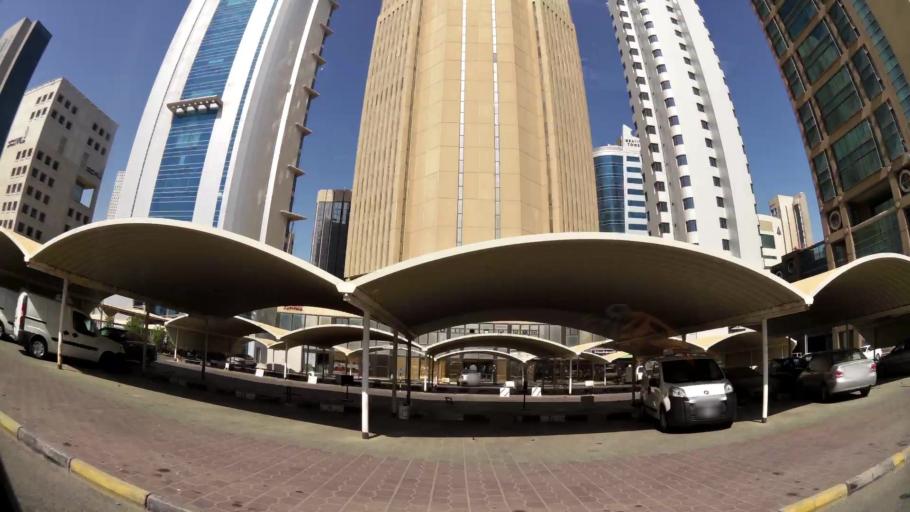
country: KW
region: Al Asimah
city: Kuwait City
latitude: 29.3810
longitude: 47.9866
